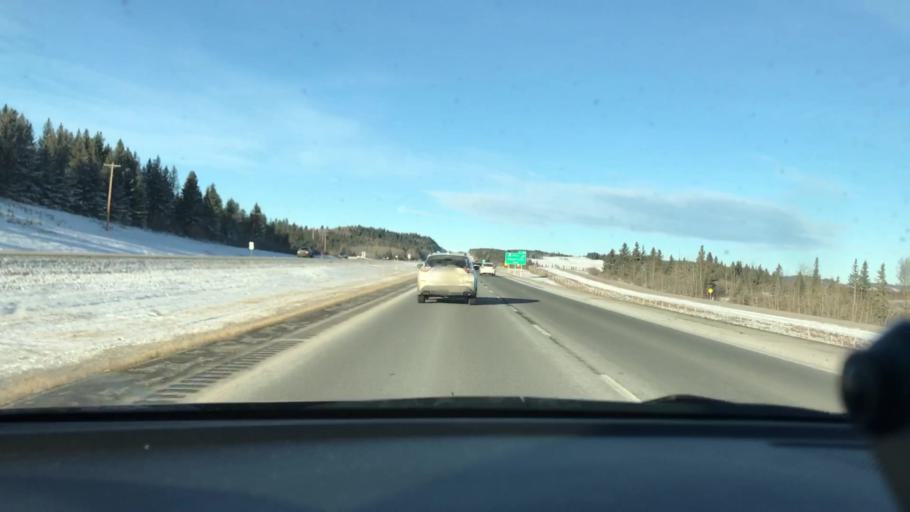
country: CA
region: Alberta
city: Cochrane
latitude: 51.1277
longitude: -114.6856
